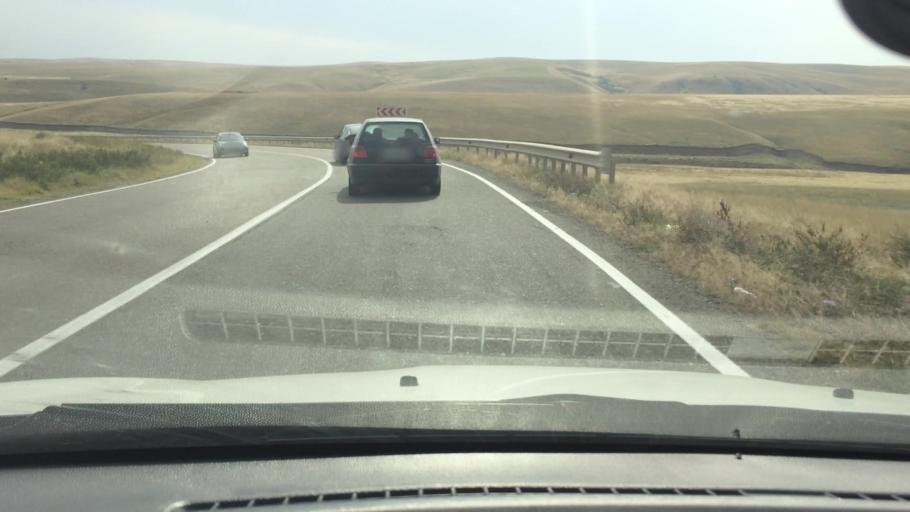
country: GE
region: Kvemo Kartli
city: Rust'avi
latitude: 41.5252
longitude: 44.9367
